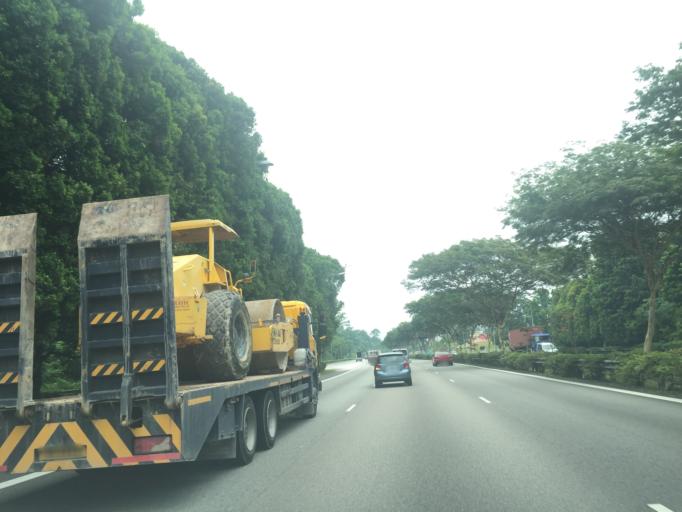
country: MY
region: Johor
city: Johor Bahru
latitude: 1.3891
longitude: 103.7586
